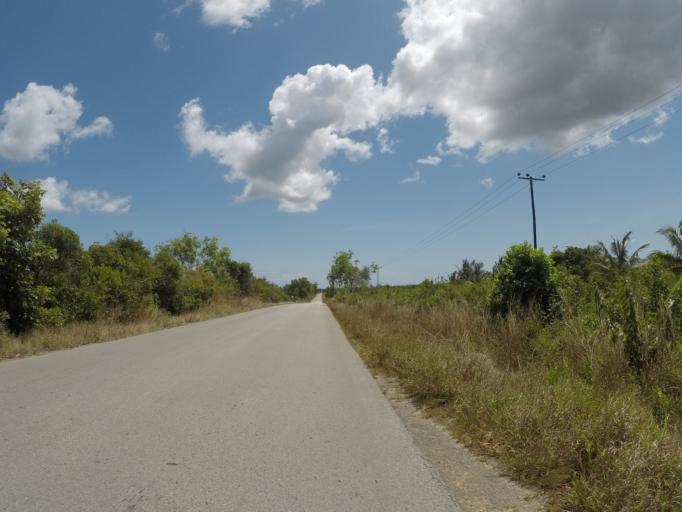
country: TZ
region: Zanzibar Central/South
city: Nganane
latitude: -6.2748
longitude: 39.4885
